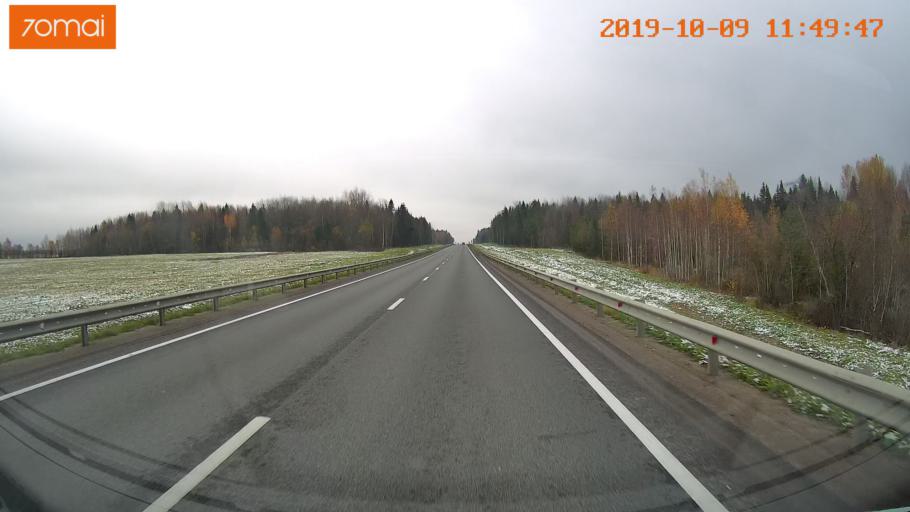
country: RU
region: Vologda
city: Gryazovets
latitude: 58.8139
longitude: 40.2358
